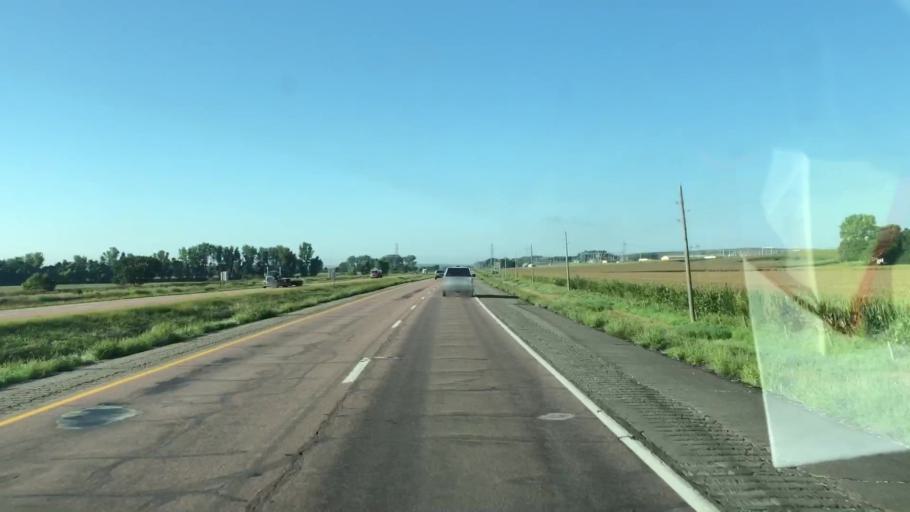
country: US
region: Iowa
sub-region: Woodbury County
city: Sioux City
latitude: 42.6118
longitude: -96.2967
